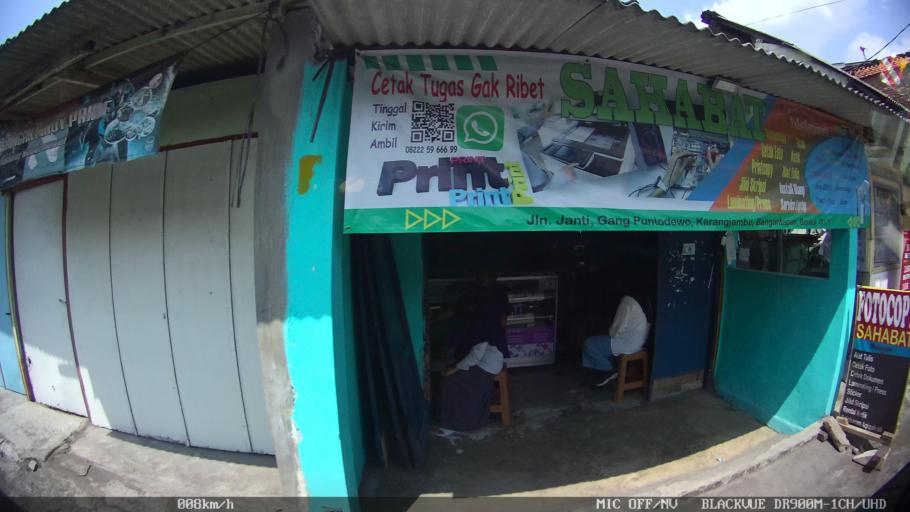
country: ID
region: Daerah Istimewa Yogyakarta
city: Depok
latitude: -7.7921
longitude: 110.4088
